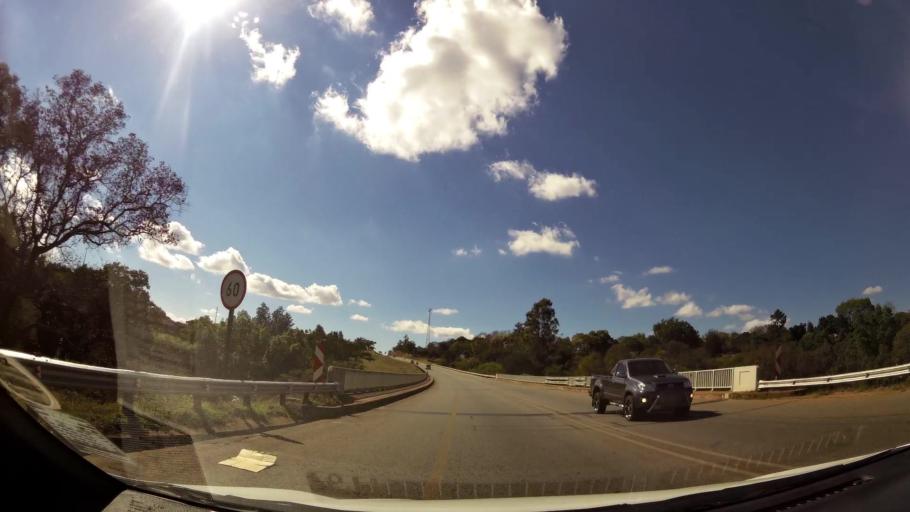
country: ZA
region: Limpopo
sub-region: Mopani District Municipality
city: Tzaneen
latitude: -23.8196
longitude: 30.1665
